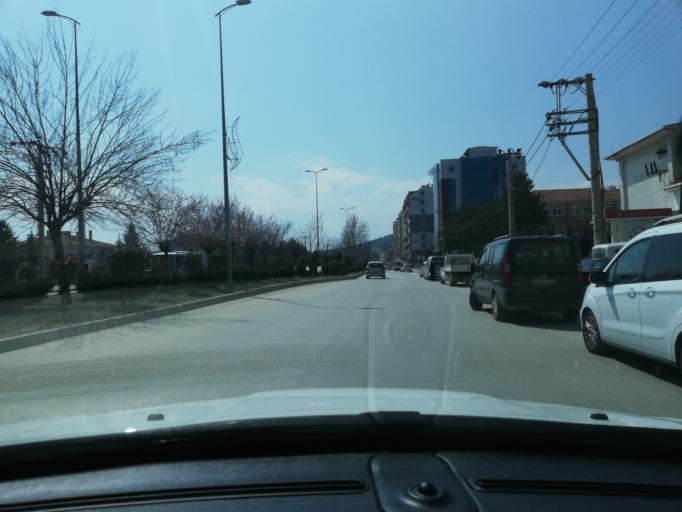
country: TR
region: Kastamonu
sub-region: Cide
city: Kastamonu
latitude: 41.4061
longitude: 33.7855
